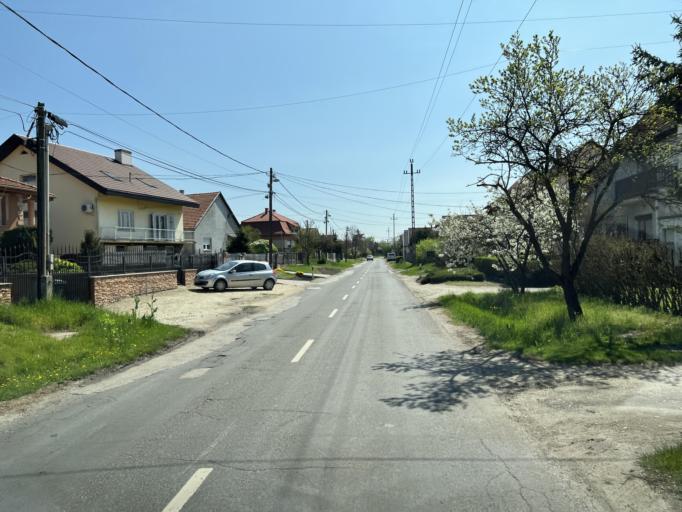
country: HU
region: Pest
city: Ocsa
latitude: 47.2975
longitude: 19.2176
